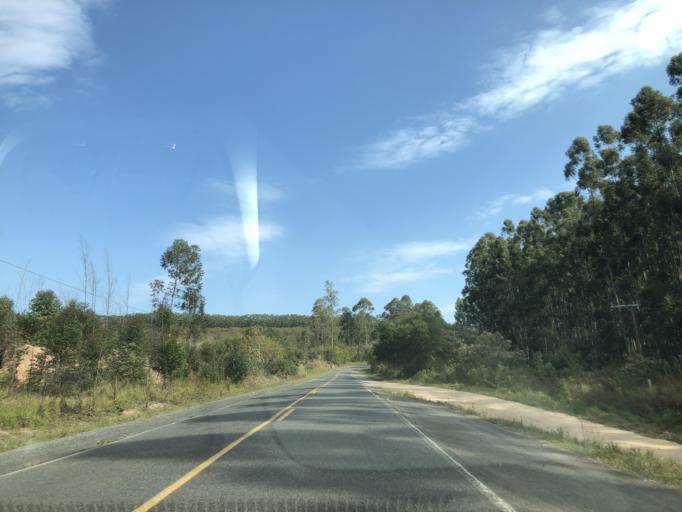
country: BR
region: Sao Paulo
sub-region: Pilar Do Sul
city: Pilar do Sul
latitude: -23.8133
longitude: -47.6460
